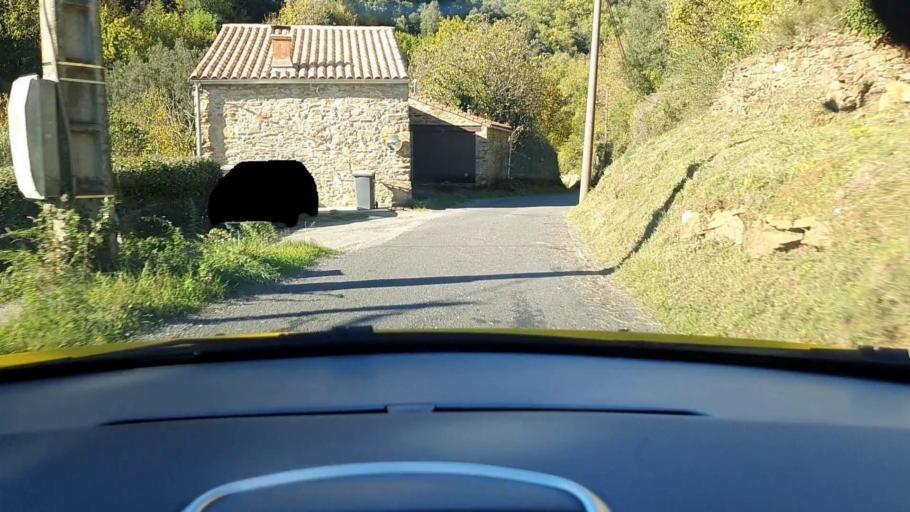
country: FR
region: Languedoc-Roussillon
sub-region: Departement du Gard
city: Le Vigan
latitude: 43.9975
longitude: 3.6199
